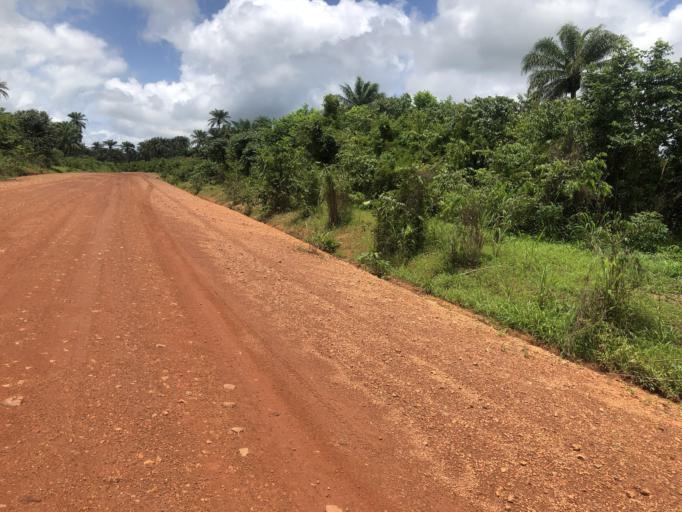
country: SL
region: Northern Province
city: Port Loko
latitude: 8.7173
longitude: -12.8364
